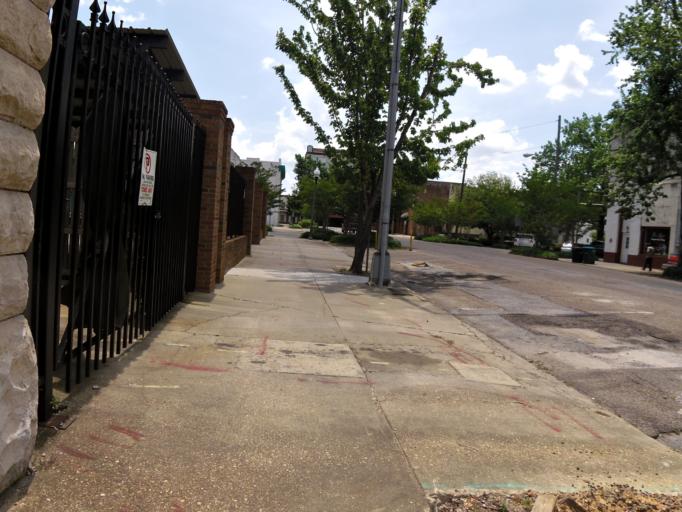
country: US
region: Mississippi
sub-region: Lauderdale County
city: Meridian
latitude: 32.3632
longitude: -88.7006
